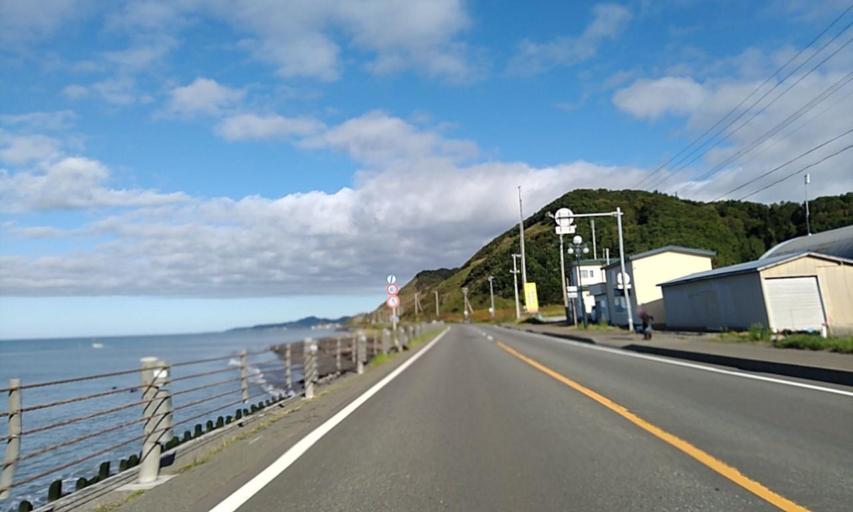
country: JP
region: Hokkaido
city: Shizunai-furukawacho
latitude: 42.2056
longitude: 142.6553
